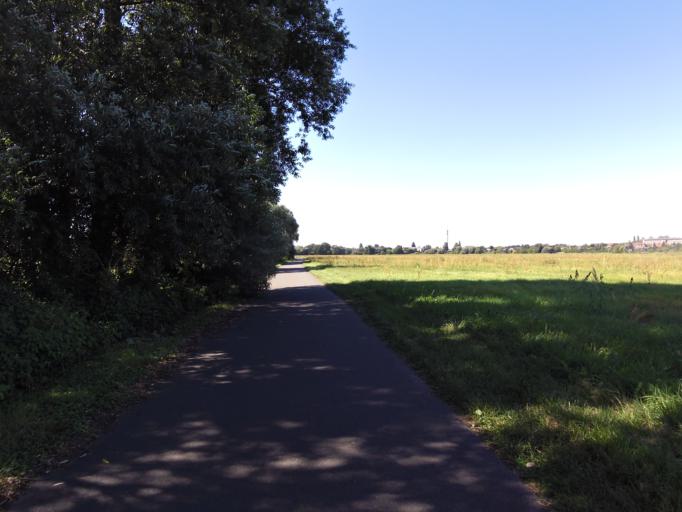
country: DE
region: Saxony-Anhalt
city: Abtsdorf
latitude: 51.8573
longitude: 12.6902
